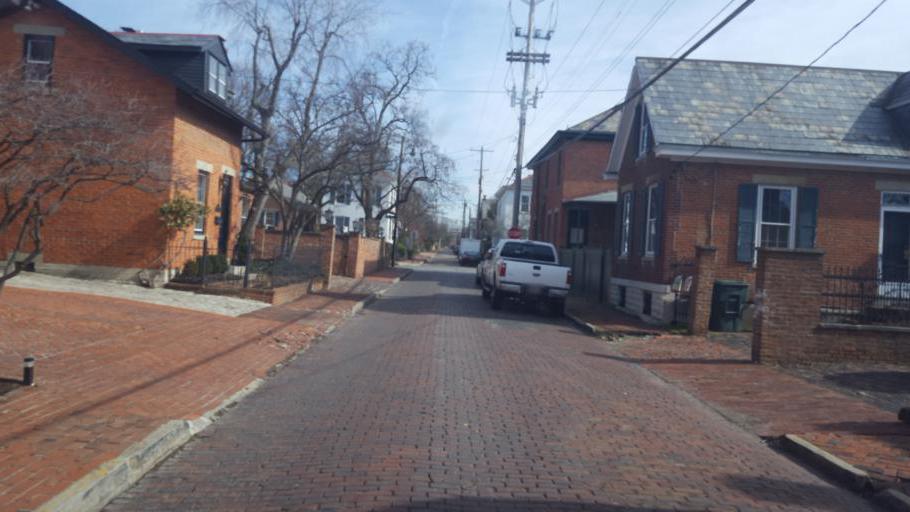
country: US
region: Ohio
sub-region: Franklin County
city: Columbus
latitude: 39.9516
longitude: -82.9915
